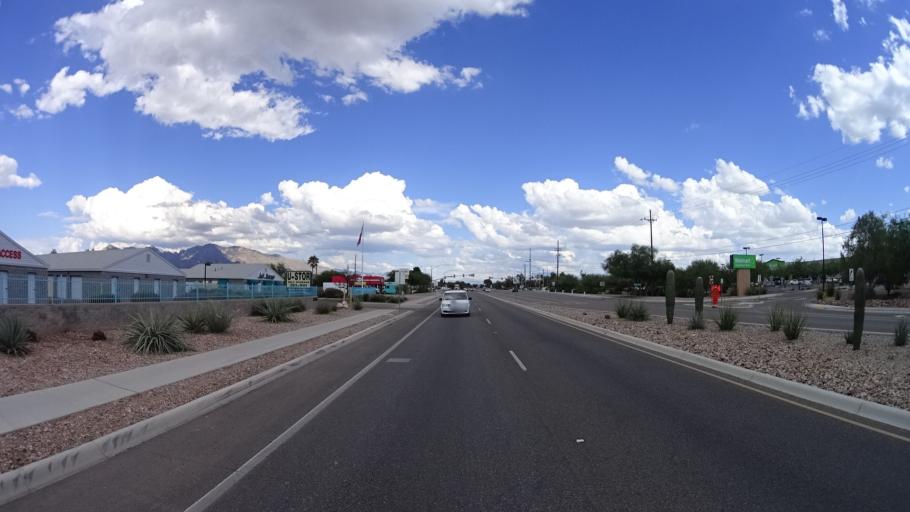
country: US
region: Arizona
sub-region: Pima County
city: Flowing Wells
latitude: 32.2944
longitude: -111.0140
